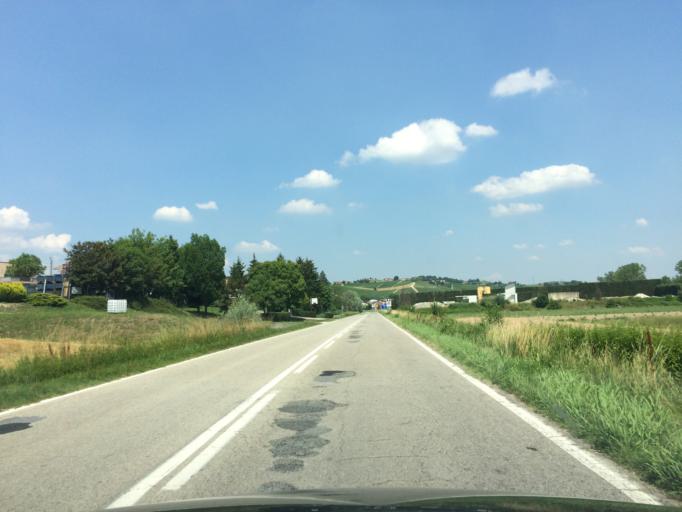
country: IT
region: Piedmont
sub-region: Provincia di Asti
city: Moasca
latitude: 44.7749
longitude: 8.2739
